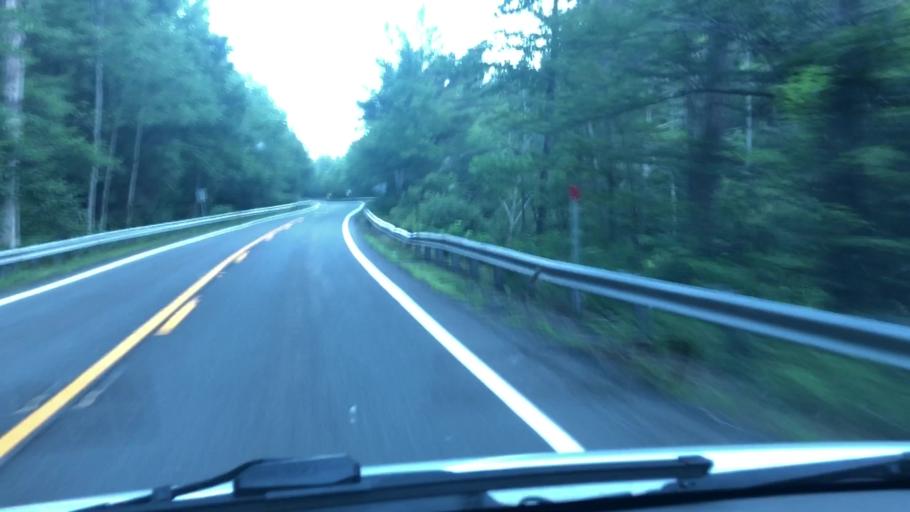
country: US
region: Massachusetts
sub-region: Hampshire County
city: Chesterfield
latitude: 42.3324
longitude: -72.8815
